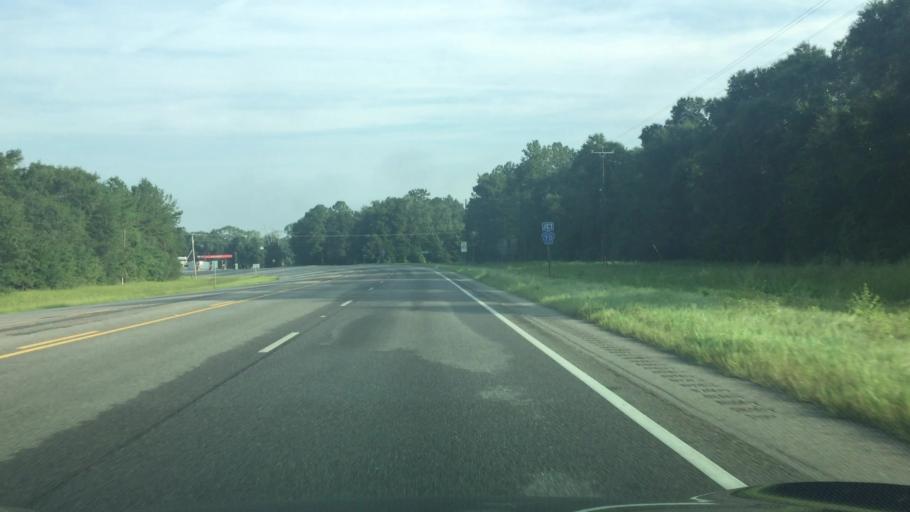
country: US
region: Alabama
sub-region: Covington County
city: Andalusia
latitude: 31.3446
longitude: -86.5247
